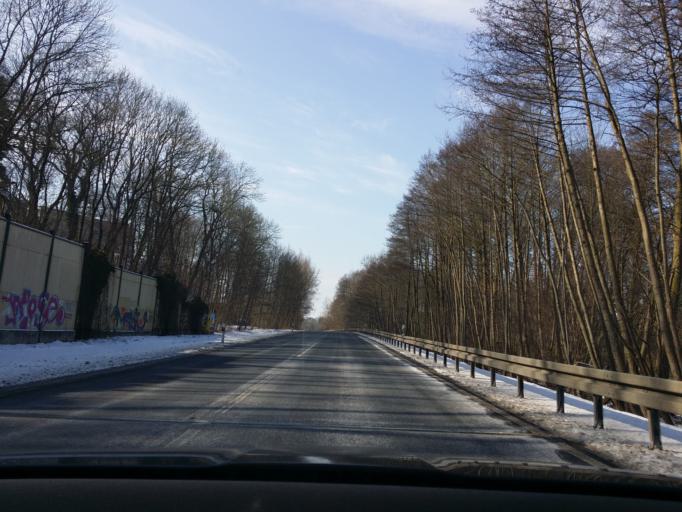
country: DE
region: Mecklenburg-Vorpommern
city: Penzlin
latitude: 53.5084
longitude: 13.0907
